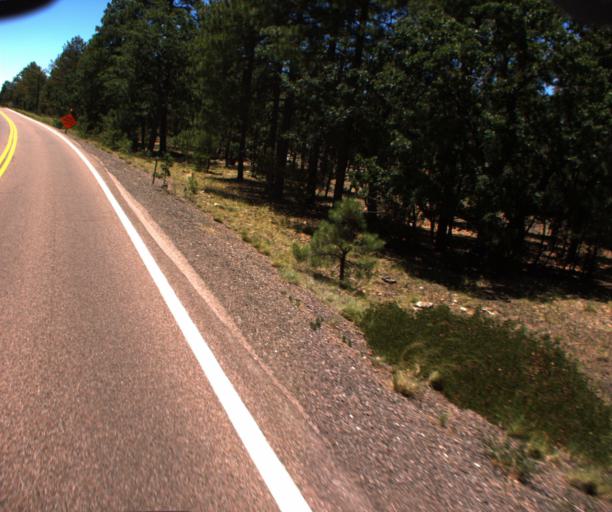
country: US
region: Arizona
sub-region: Gila County
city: Pine
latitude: 34.4411
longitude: -111.4920
